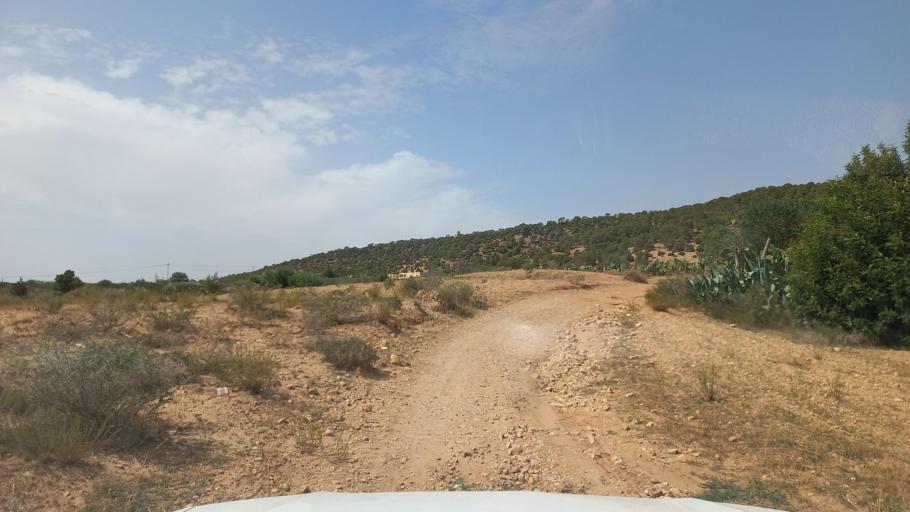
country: TN
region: Al Qasrayn
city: Kasserine
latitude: 35.3779
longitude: 8.9118
